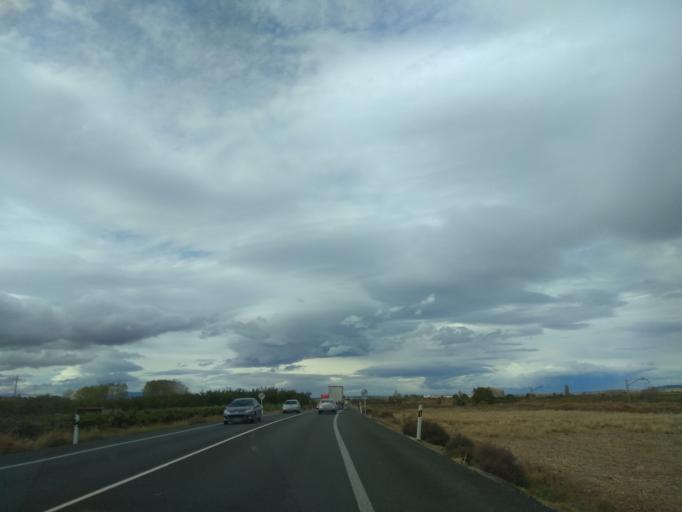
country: ES
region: La Rioja
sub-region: Provincia de La Rioja
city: Rincon de Soto
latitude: 42.2143
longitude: -1.8155
